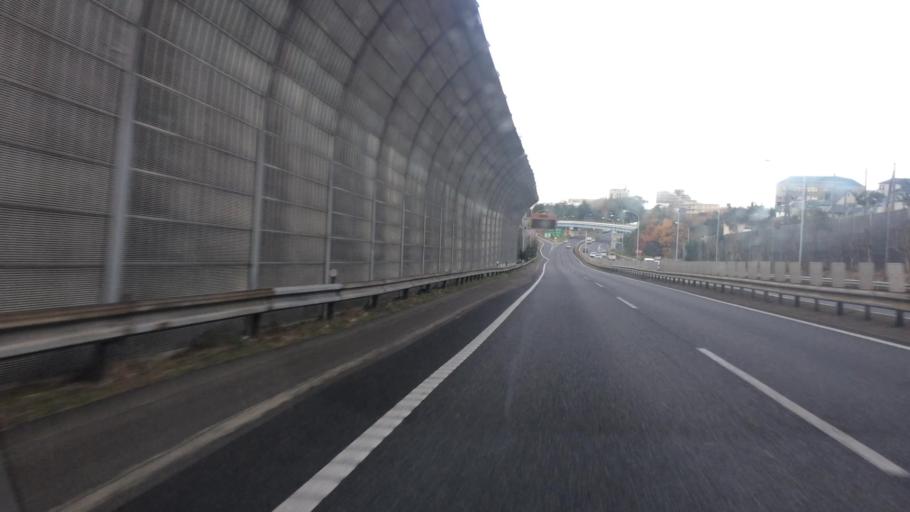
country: JP
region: Hyogo
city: Akashi
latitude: 34.6590
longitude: 135.0312
